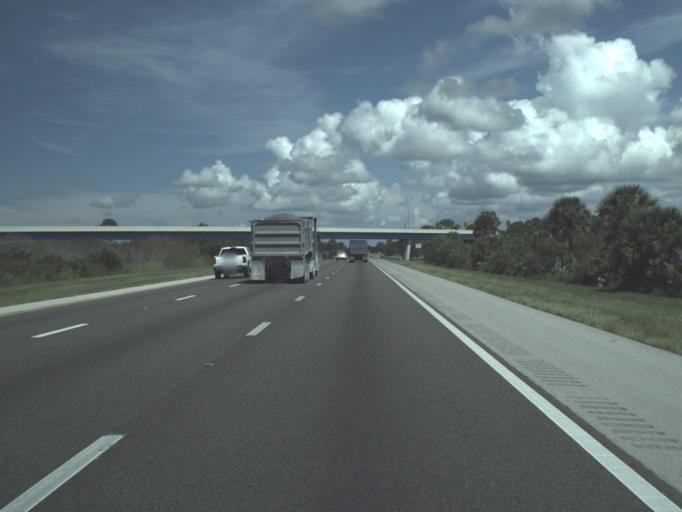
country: US
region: Florida
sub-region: Sarasota County
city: Laurel
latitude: 27.1891
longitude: -82.4375
